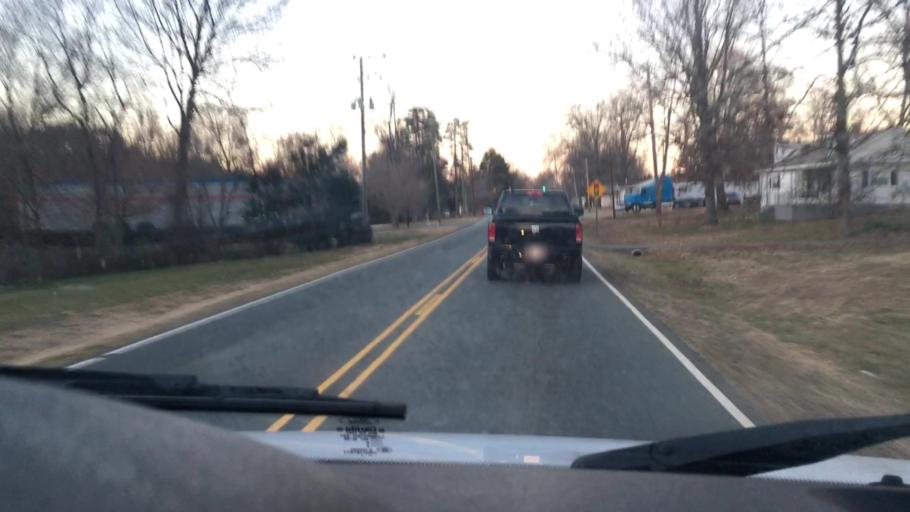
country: US
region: North Carolina
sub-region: Mecklenburg County
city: Huntersville
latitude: 35.4243
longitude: -80.8424
